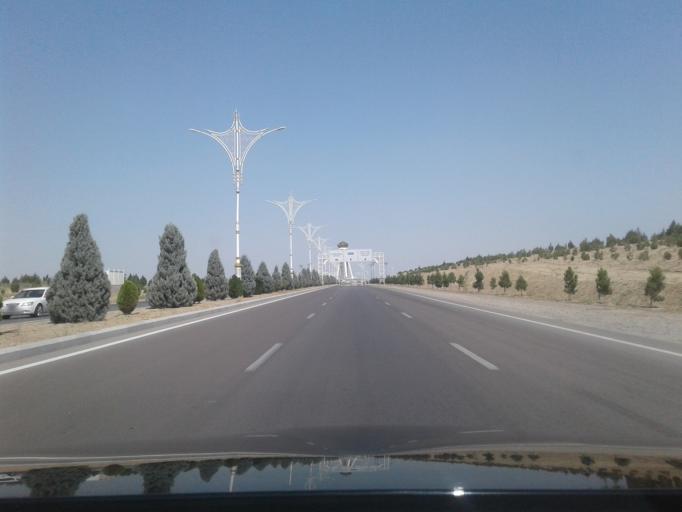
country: TM
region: Ahal
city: Ashgabat
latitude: 37.8781
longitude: 58.4164
